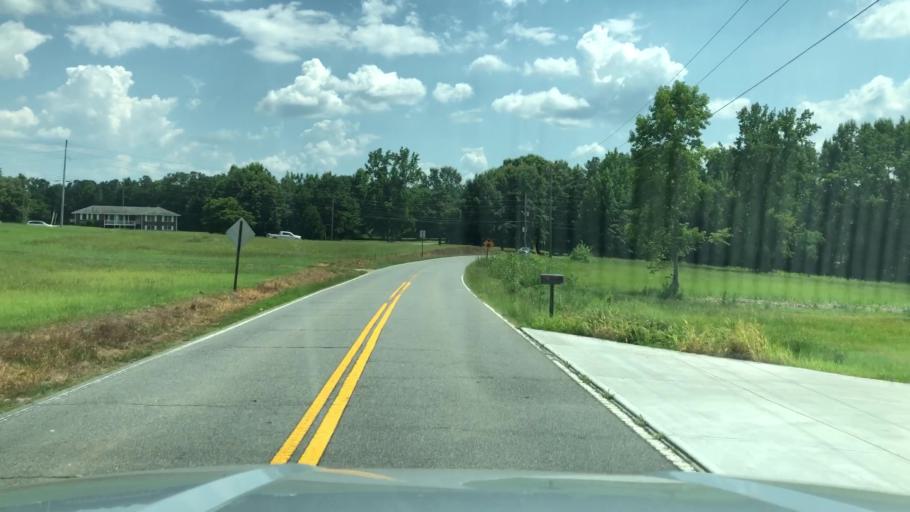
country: US
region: Georgia
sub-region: Cobb County
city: Acworth
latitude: 33.9757
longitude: -84.7189
